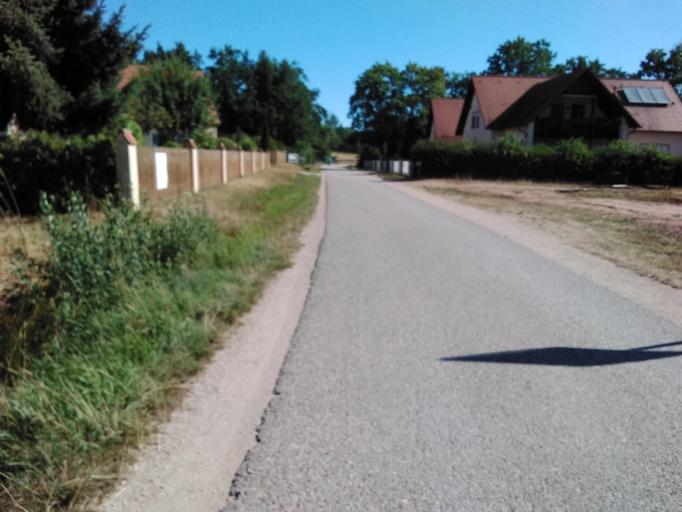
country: DE
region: Bavaria
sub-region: Regierungsbezirk Mittelfranken
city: Allersberg
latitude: 49.2392
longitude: 11.2048
